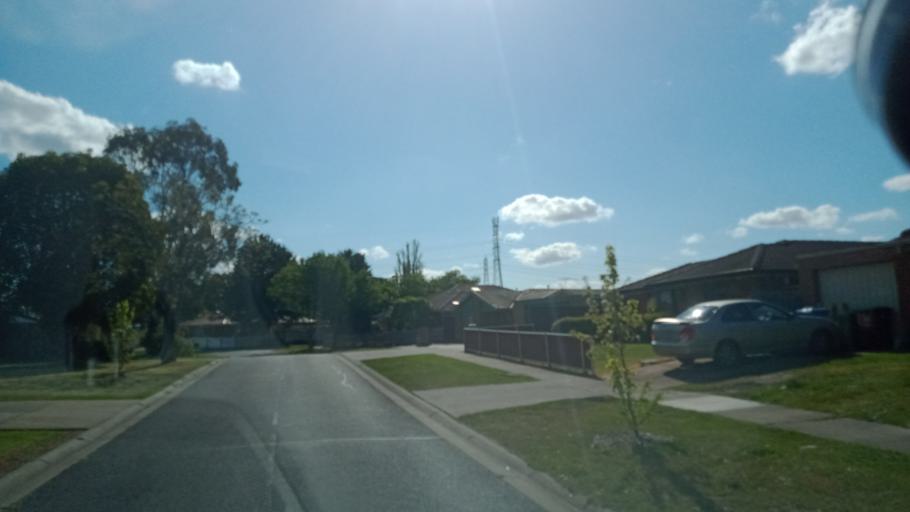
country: AU
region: Victoria
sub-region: Casey
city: Cranbourne West
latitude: -38.0979
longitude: 145.2674
